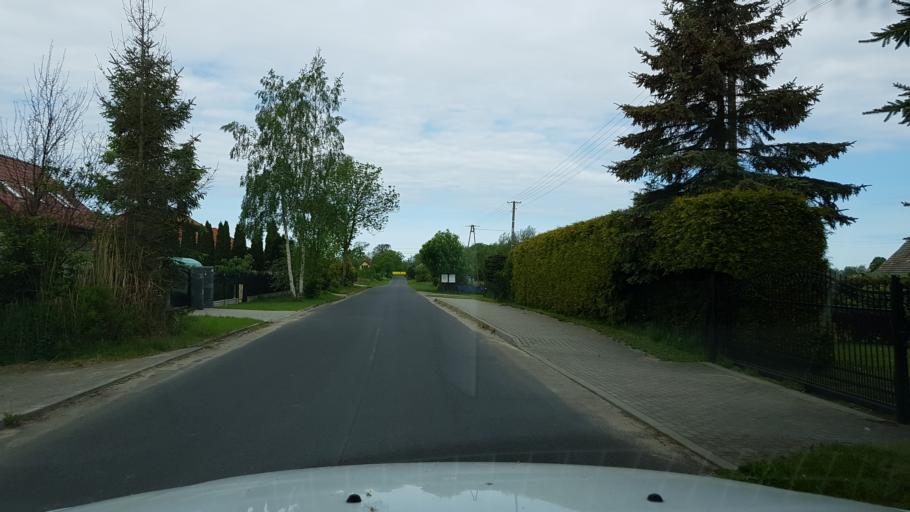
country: PL
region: West Pomeranian Voivodeship
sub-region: Powiat kolobrzeski
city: Ustronie Morskie
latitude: 54.2193
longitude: 15.8113
